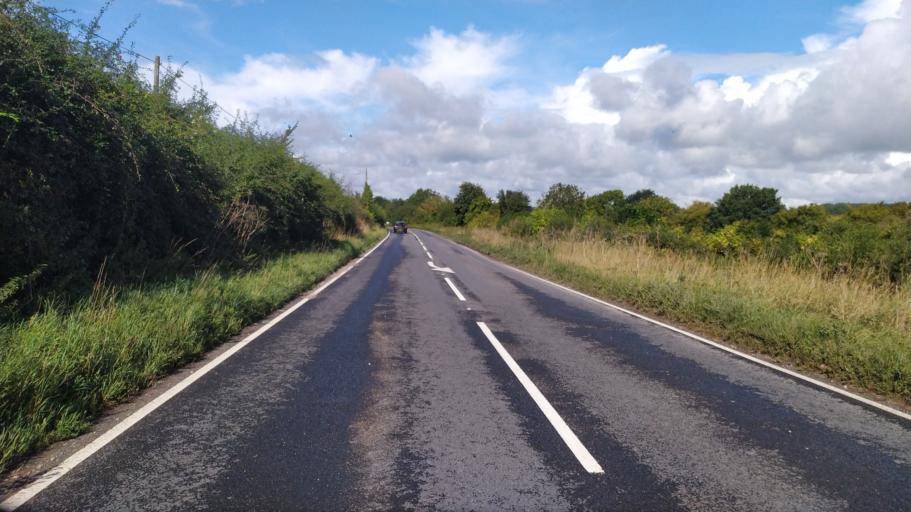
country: GB
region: England
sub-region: Dorset
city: Manston
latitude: 50.8906
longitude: -2.2308
